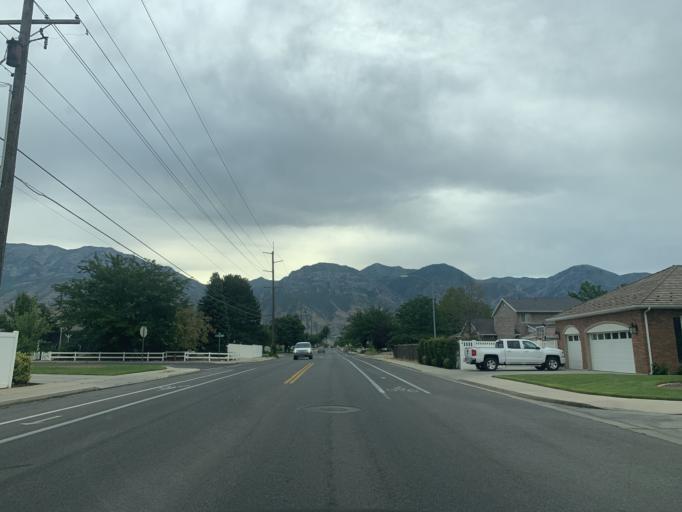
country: US
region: Utah
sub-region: Utah County
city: Provo
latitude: 40.2534
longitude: -111.6924
